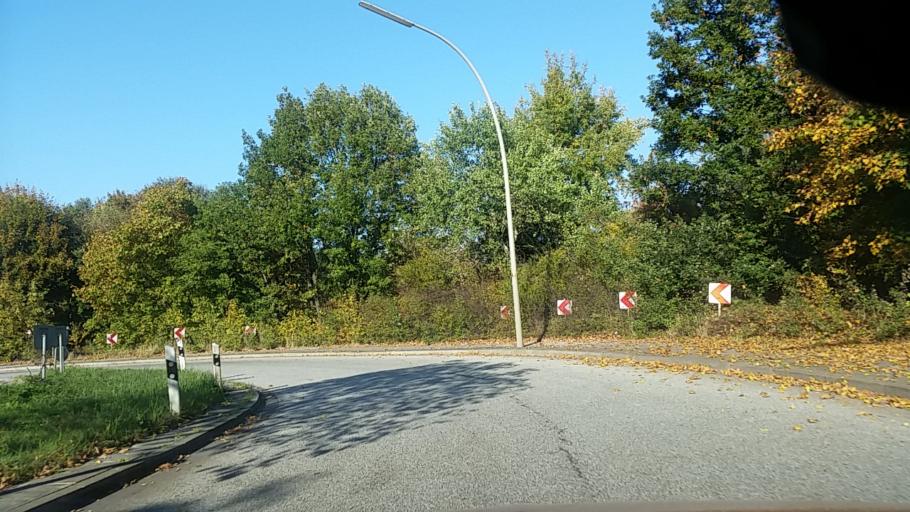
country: DE
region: Schleswig-Holstein
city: Oststeinbek
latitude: 53.4895
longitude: 10.1168
